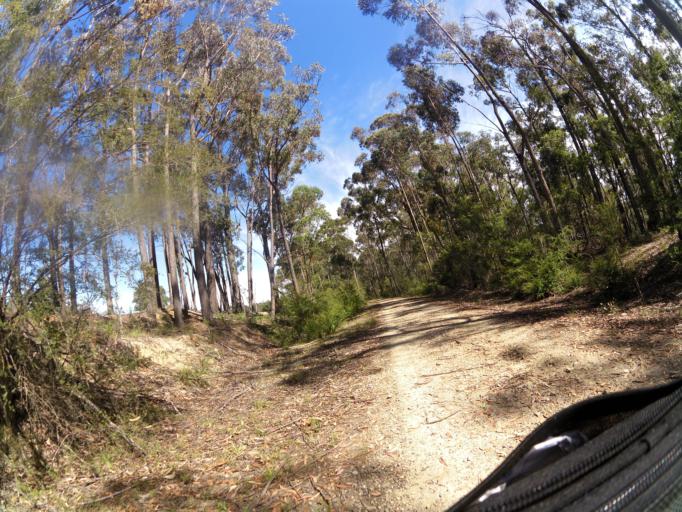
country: AU
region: Victoria
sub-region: East Gippsland
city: Lakes Entrance
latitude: -37.7200
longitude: 148.1440
